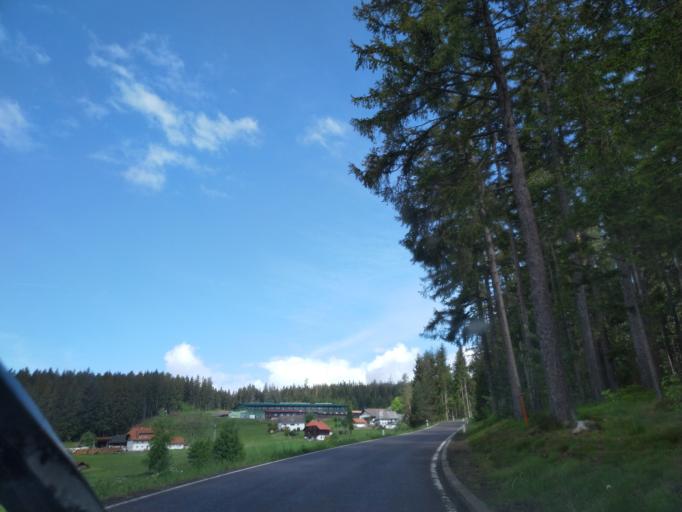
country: DE
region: Baden-Wuerttemberg
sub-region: Freiburg Region
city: Friedenweiler
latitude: 47.9358
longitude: 8.2514
